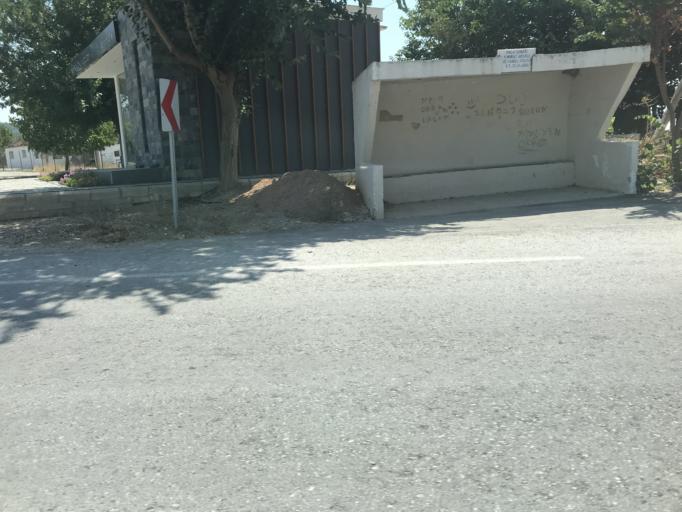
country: TR
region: Izmir
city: Urla
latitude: 38.2810
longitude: 26.7449
